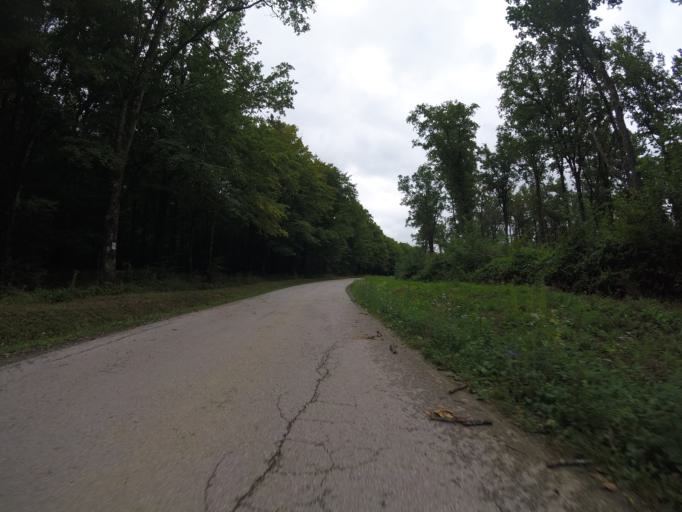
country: HR
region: Zagrebacka
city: Mraclin
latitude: 45.6164
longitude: 16.0941
